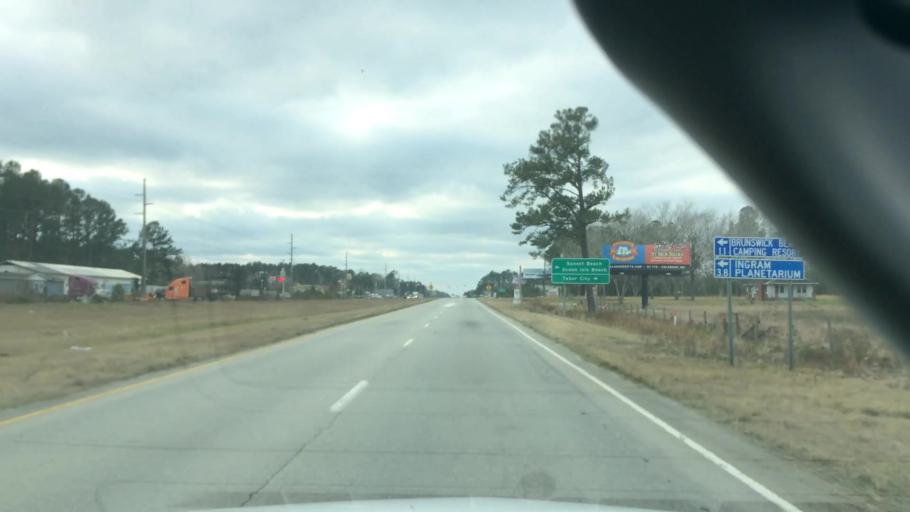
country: US
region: North Carolina
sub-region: Brunswick County
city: Sunset Beach
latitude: 33.9472
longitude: -78.4981
